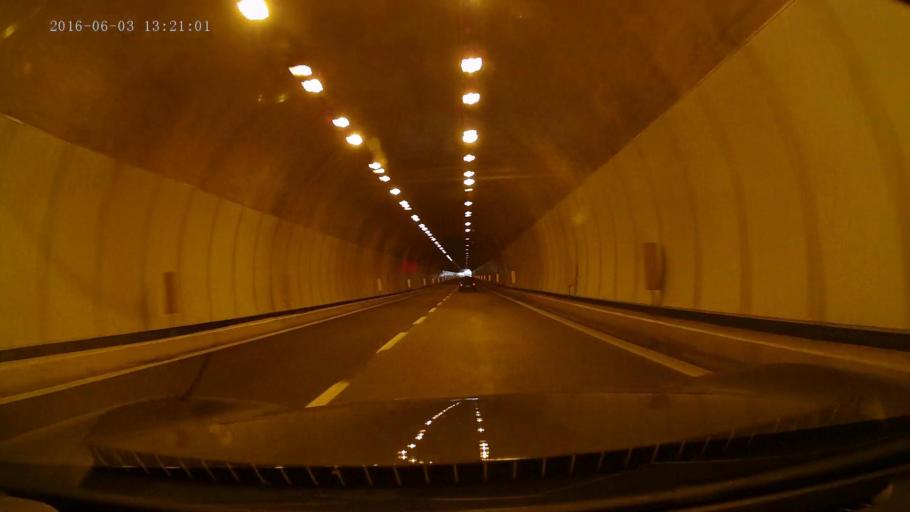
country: IT
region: Trentino-Alto Adige
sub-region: Bolzano
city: Fie Allo Sciliar
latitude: 46.5254
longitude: 11.4872
